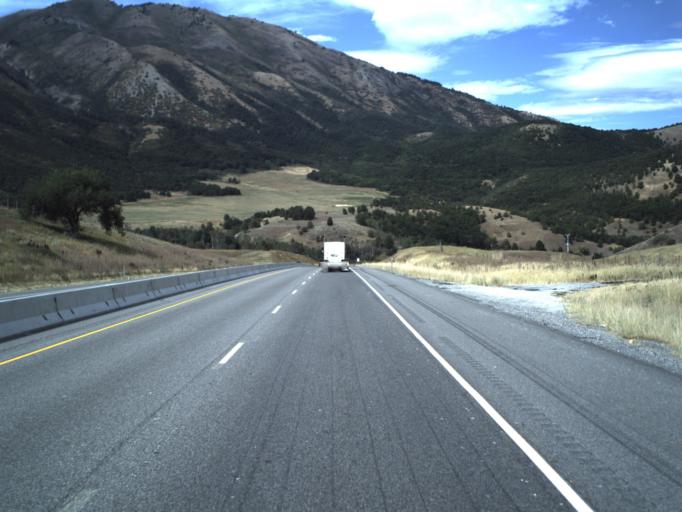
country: US
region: Utah
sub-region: Cache County
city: Wellsville
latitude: 41.5955
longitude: -111.9786
